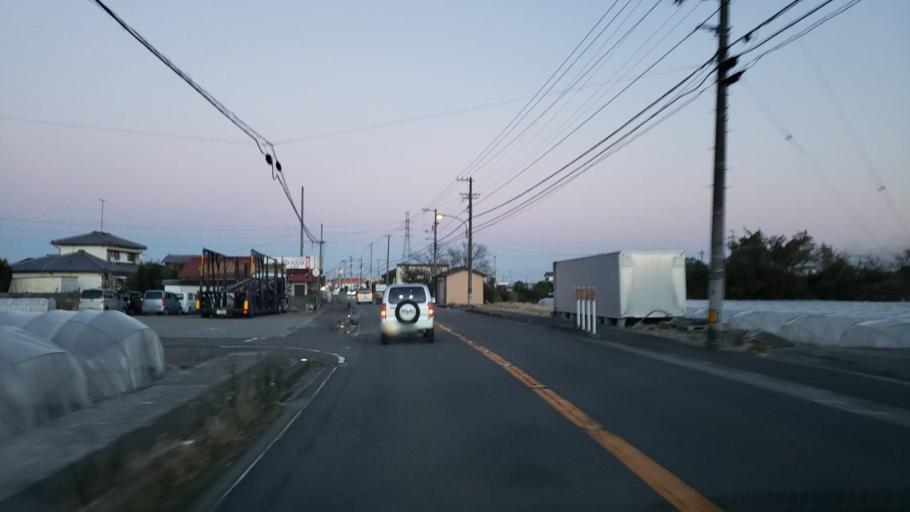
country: JP
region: Tokushima
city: Ishii
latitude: 34.1203
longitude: 134.4402
